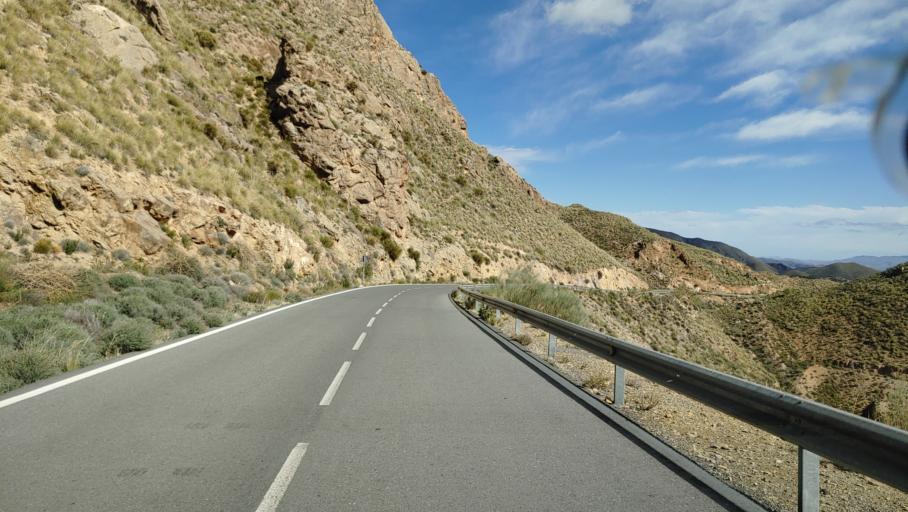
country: ES
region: Andalusia
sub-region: Provincia de Almeria
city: Canjayar
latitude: 37.0250
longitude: -2.7287
